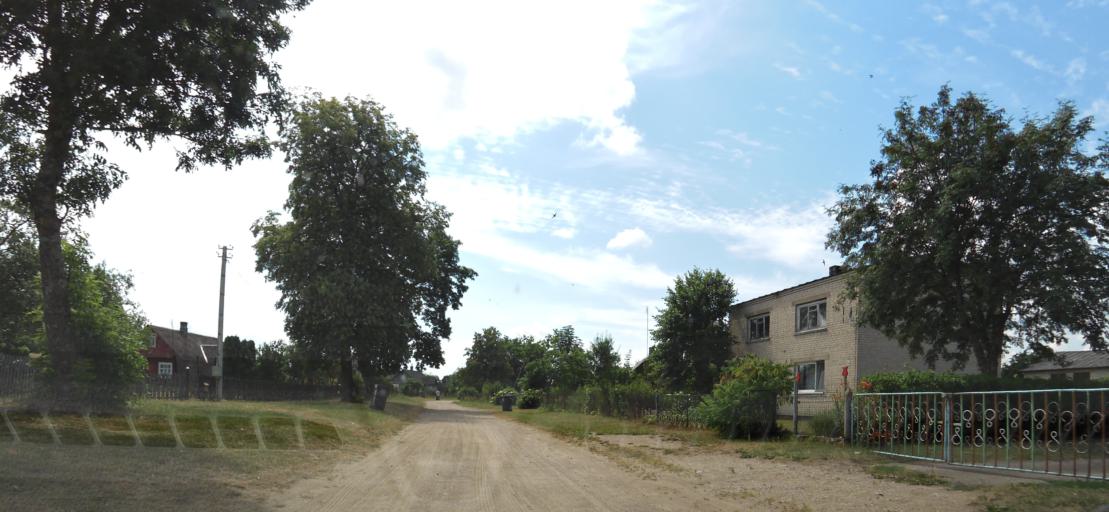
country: LT
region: Vilnius County
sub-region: Trakai
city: Rudiskes
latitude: 54.2983
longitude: 24.7853
